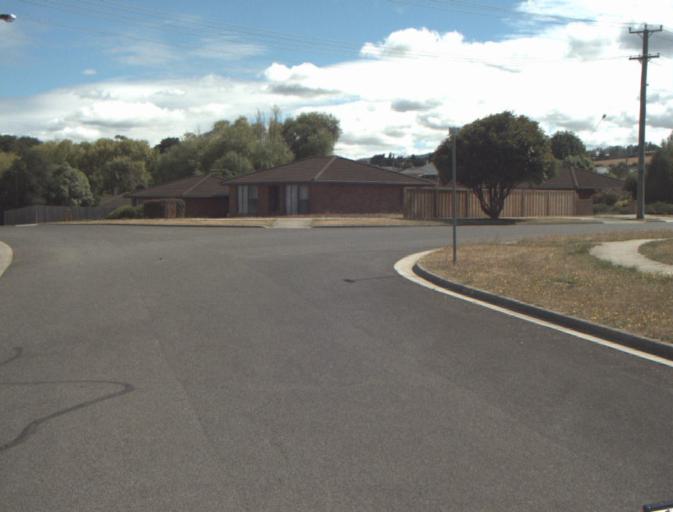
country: AU
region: Tasmania
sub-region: Launceston
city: Mayfield
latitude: -41.3861
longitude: 147.1108
